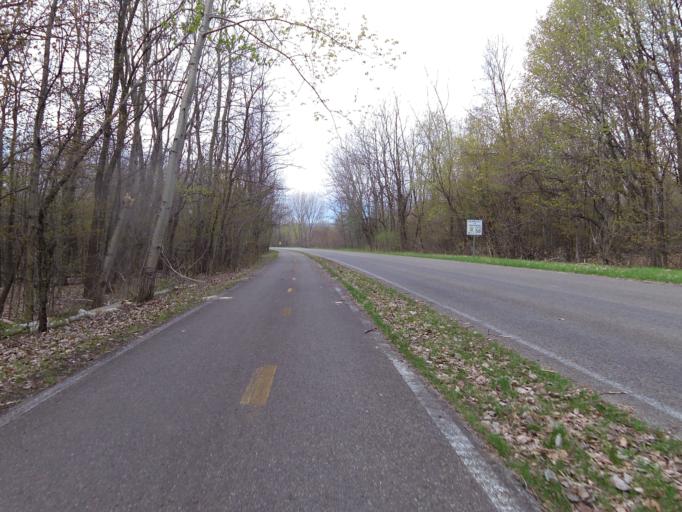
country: CA
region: Quebec
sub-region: Laurentides
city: Oka
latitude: 45.4908
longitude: -74.0143
